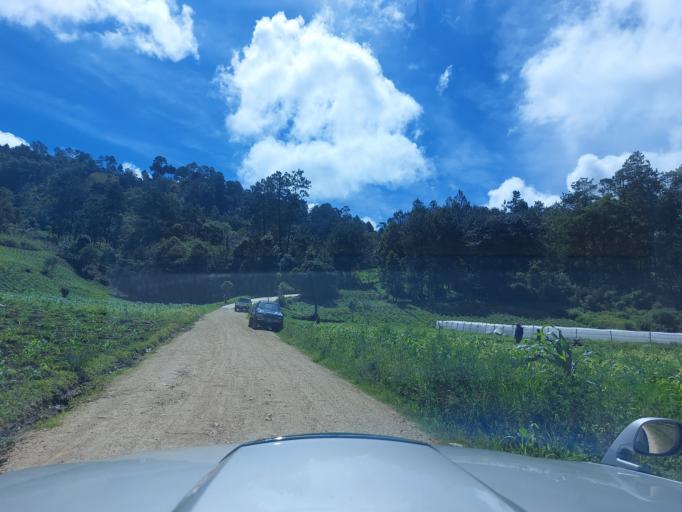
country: GT
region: Chimaltenango
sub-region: Municipio de San Juan Comalapa
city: Comalapa
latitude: 14.7527
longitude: -90.8687
